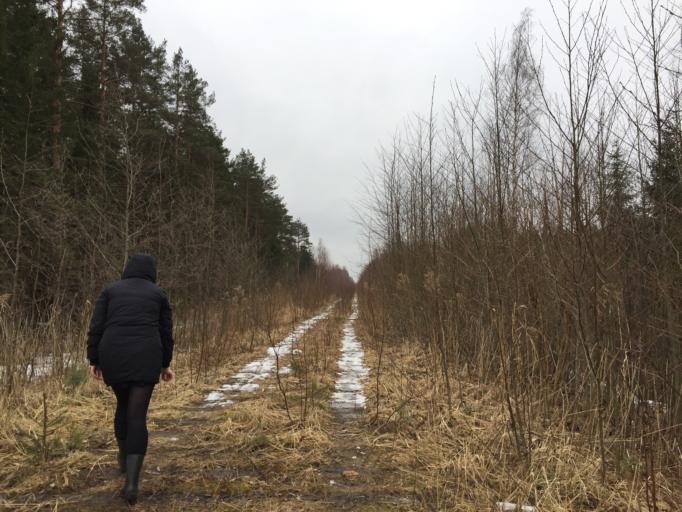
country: LV
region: Lielvarde
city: Lielvarde
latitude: 56.7628
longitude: 24.8190
